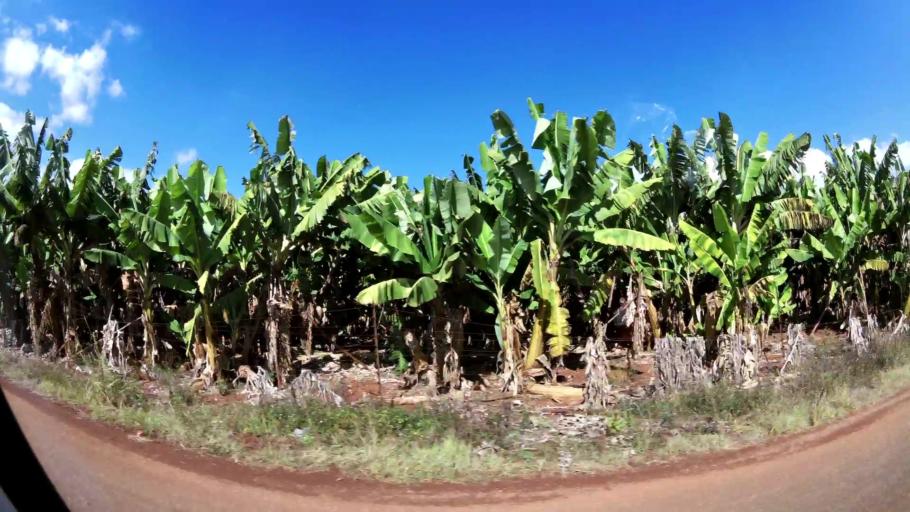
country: ZA
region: Limpopo
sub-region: Mopani District Municipality
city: Tzaneen
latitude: -23.7999
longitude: 30.1328
